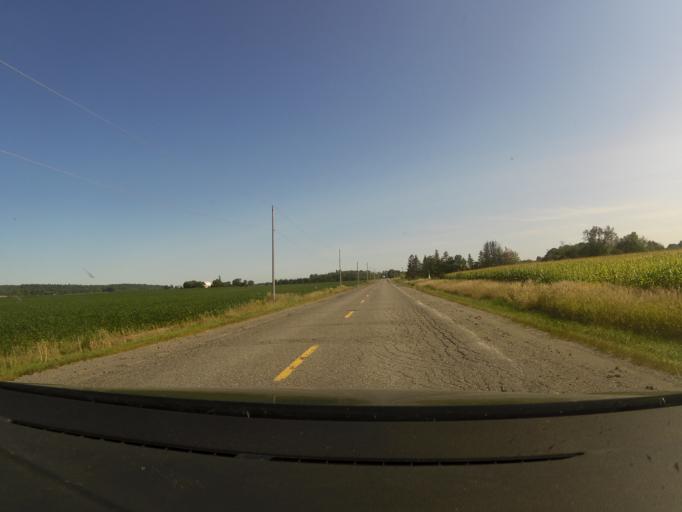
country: CA
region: Ontario
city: Arnprior
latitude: 45.3742
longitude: -76.1190
